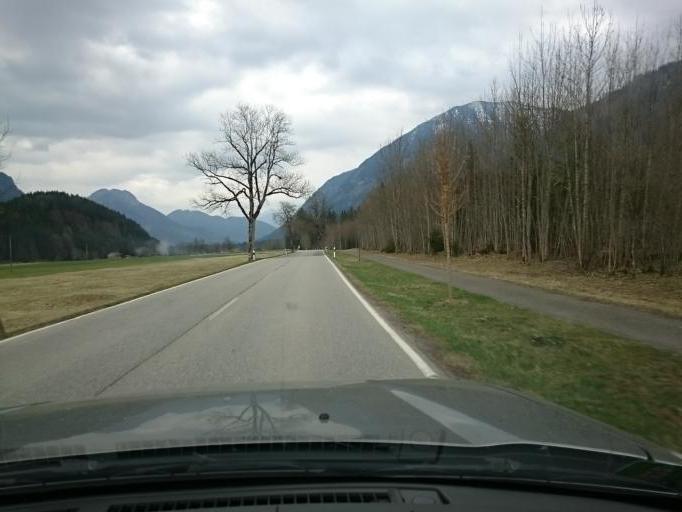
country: DE
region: Bavaria
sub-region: Upper Bavaria
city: Unterammergau
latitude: 47.5699
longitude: 11.0075
